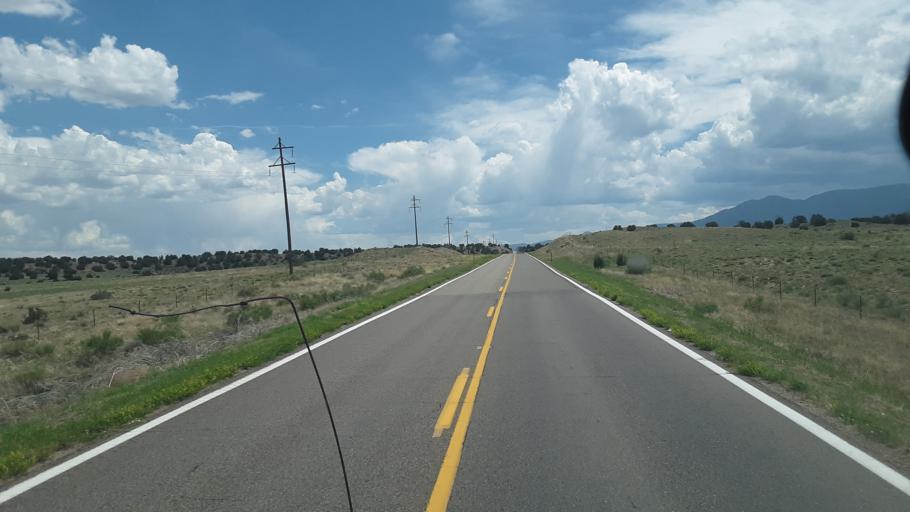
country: US
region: Colorado
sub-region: Fremont County
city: Florence
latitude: 38.3370
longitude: -105.1063
